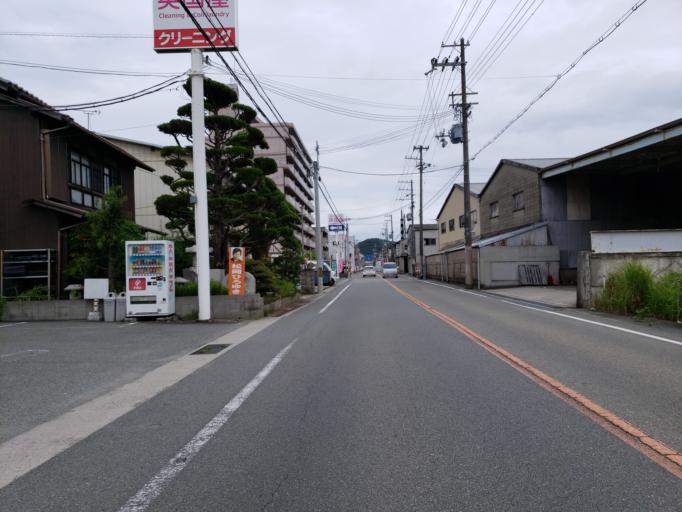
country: JP
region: Hyogo
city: Shirahamacho-usazakiminami
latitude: 34.7861
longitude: 134.7122
